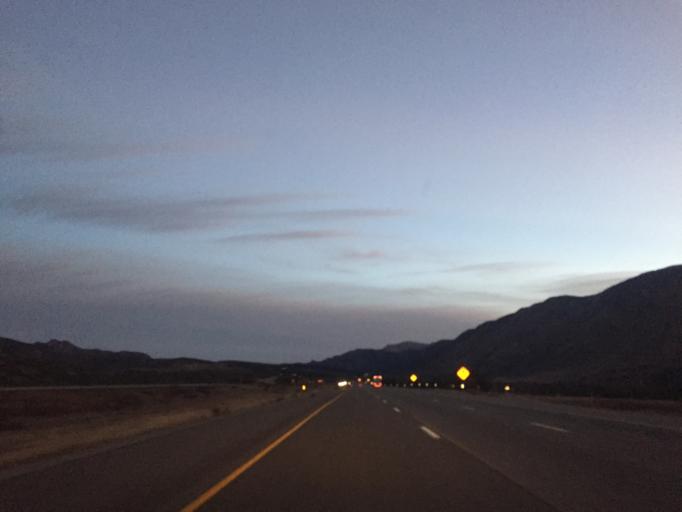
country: US
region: Utah
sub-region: Washington County
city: Toquerville
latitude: 37.3210
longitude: -113.2887
